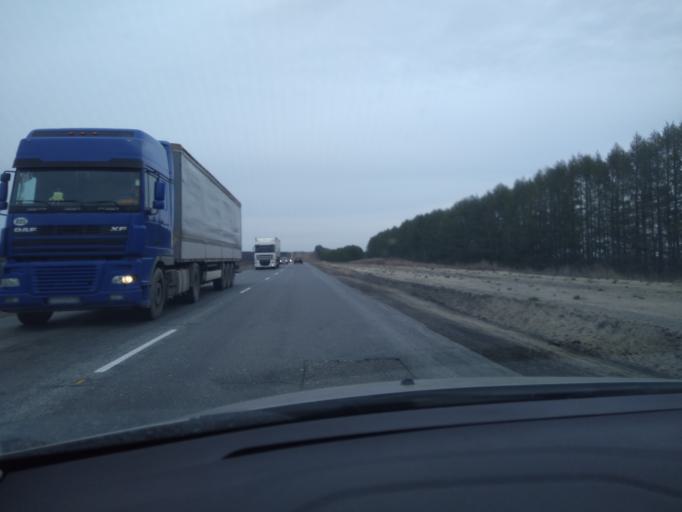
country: RU
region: Sverdlovsk
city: Kamyshlov
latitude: 56.8571
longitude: 62.8857
